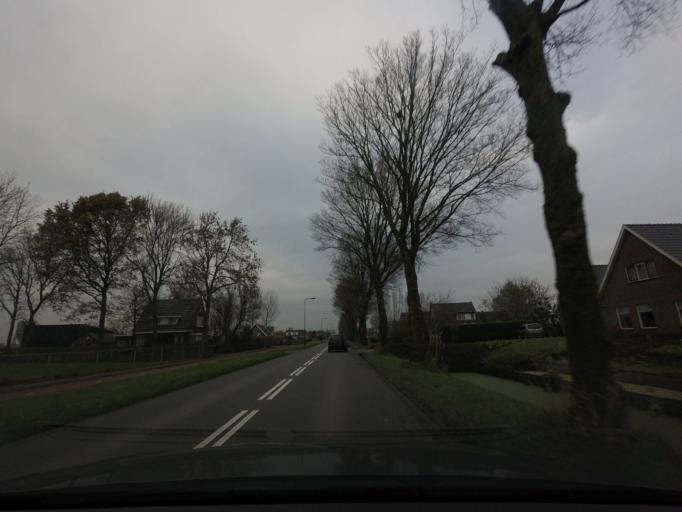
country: NL
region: North Holland
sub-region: Gemeente Heerhugowaard
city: Heerhugowaard
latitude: 52.6911
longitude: 4.8504
